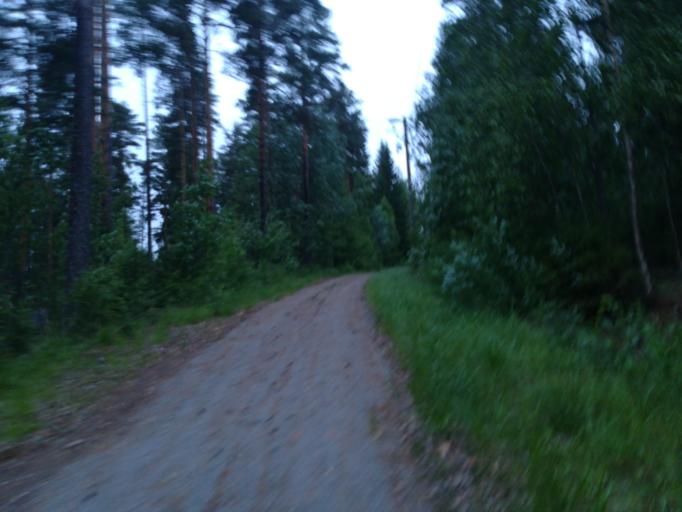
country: FI
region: Southern Savonia
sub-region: Mikkeli
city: Ristiina
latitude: 61.4844
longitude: 27.2823
